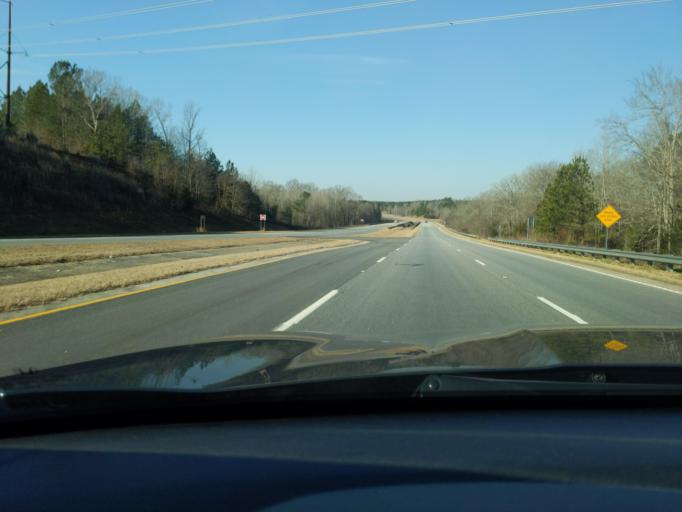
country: US
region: South Carolina
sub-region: Abbeville County
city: Calhoun Falls
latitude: 34.1108
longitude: -82.5068
